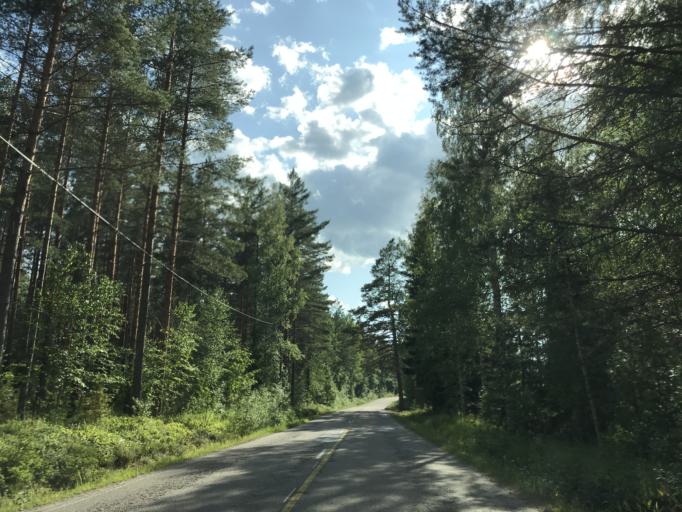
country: FI
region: Uusimaa
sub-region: Helsinki
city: Vihti
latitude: 60.4378
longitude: 24.5480
